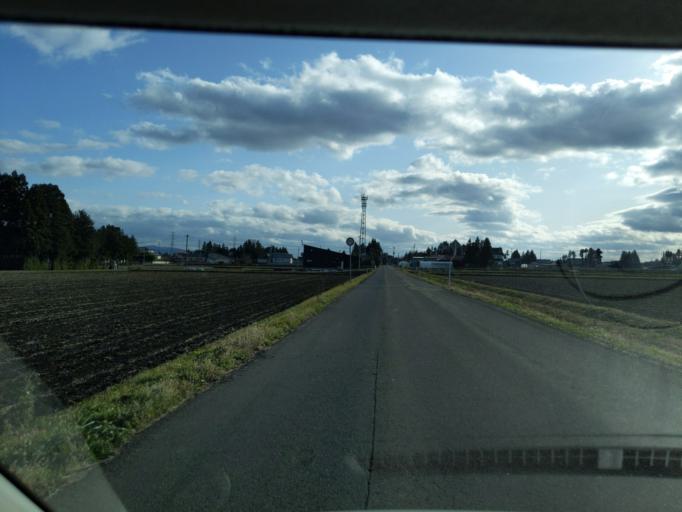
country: JP
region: Iwate
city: Mizusawa
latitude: 39.1426
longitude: 141.0792
